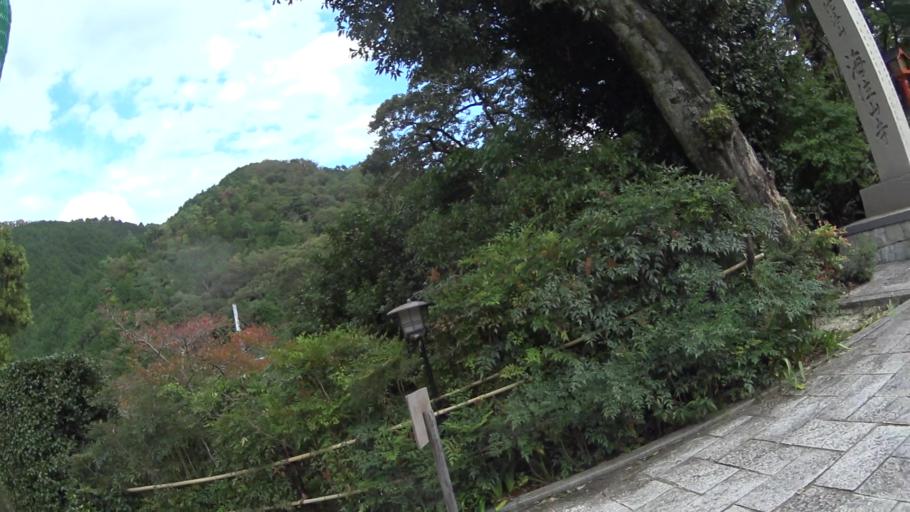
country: JP
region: Kyoto
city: Tanabe
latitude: 34.7792
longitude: 135.8592
